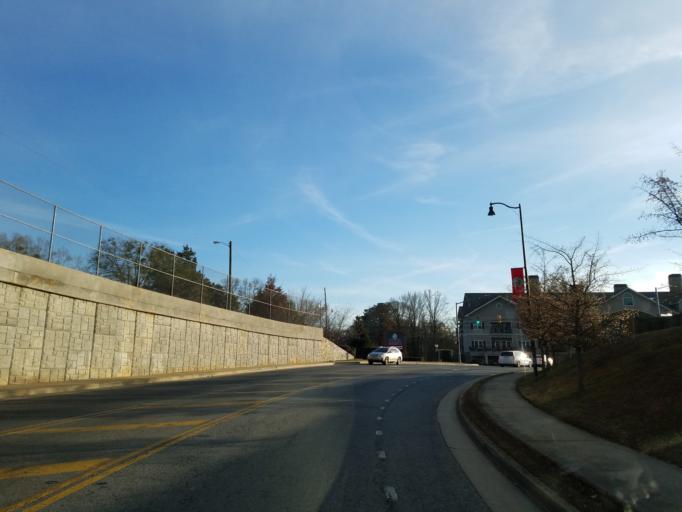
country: US
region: Georgia
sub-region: Cobb County
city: Acworth
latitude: 34.0644
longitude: -84.6668
